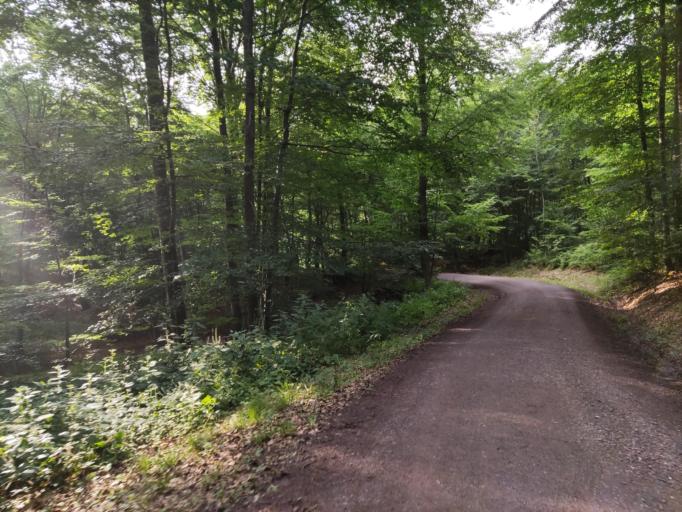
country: DE
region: Saarland
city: Nalbach
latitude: 49.4399
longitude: 6.7834
